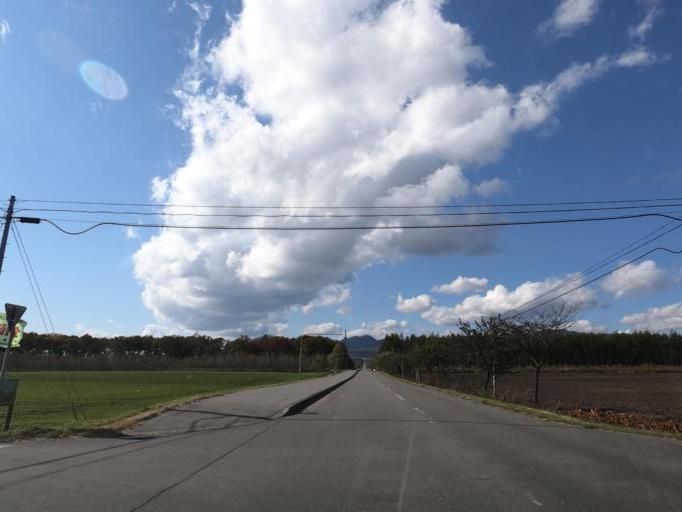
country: JP
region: Hokkaido
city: Otofuke
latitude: 43.2415
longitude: 143.2559
